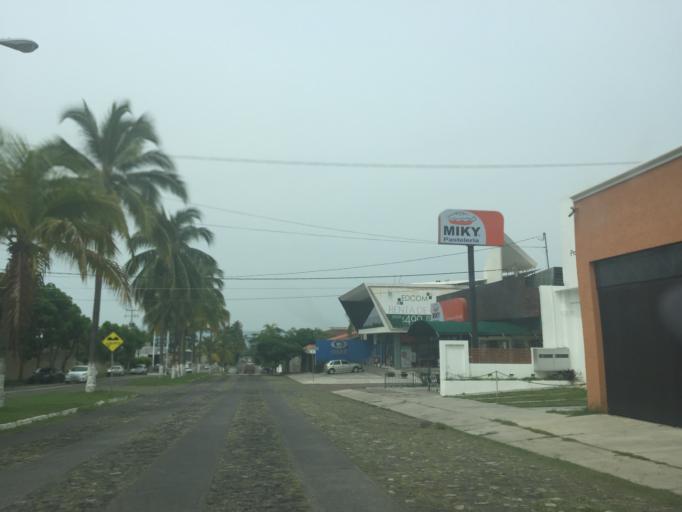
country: MX
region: Colima
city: Colima
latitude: 19.2596
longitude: -103.7143
